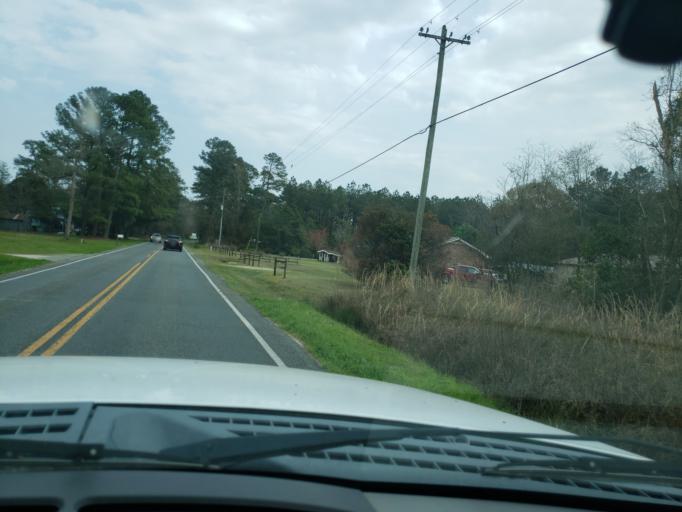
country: US
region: North Carolina
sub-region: Duplin County
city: Beulaville
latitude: 34.7581
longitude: -77.7921
